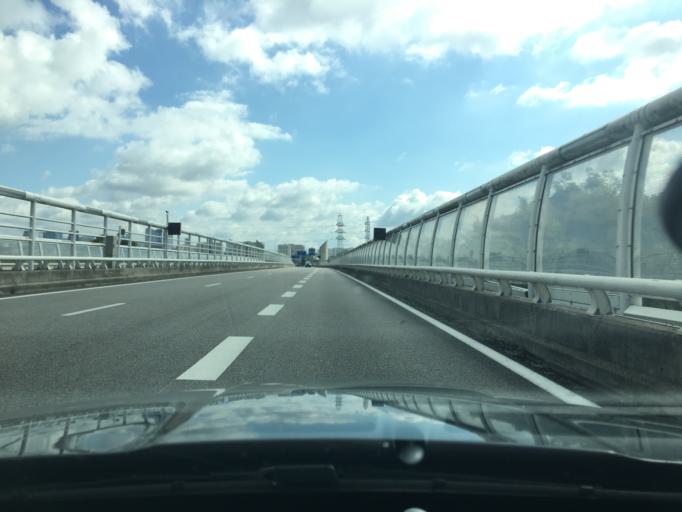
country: FR
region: Ile-de-France
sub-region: Departement des Yvelines
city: Carrieres-sur-Seine
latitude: 48.9069
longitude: 2.1928
